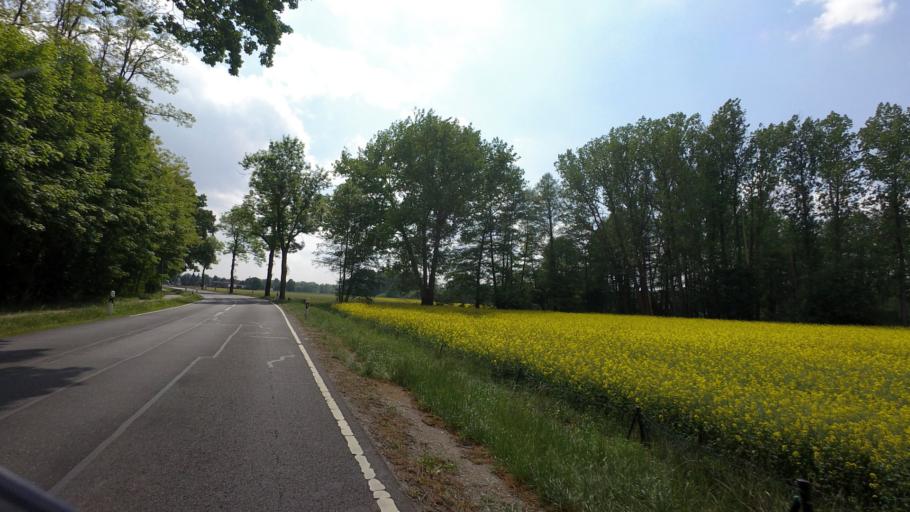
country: DE
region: Saxony
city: Rietschen
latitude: 51.4078
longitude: 14.7870
